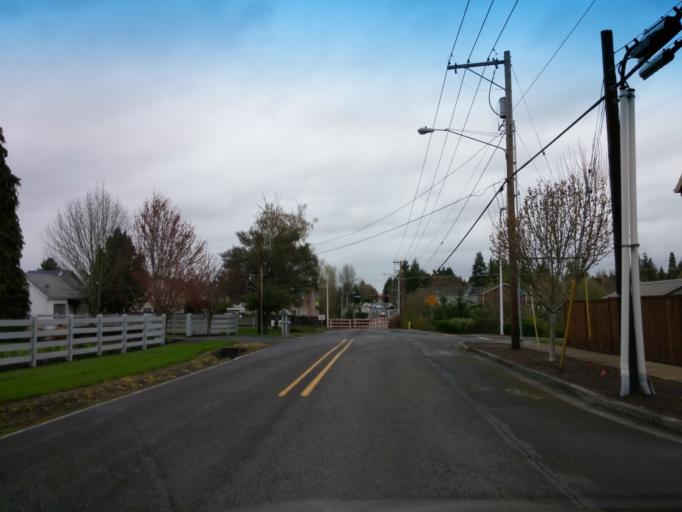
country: US
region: Oregon
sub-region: Washington County
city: Oak Hills
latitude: 45.5201
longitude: -122.8548
